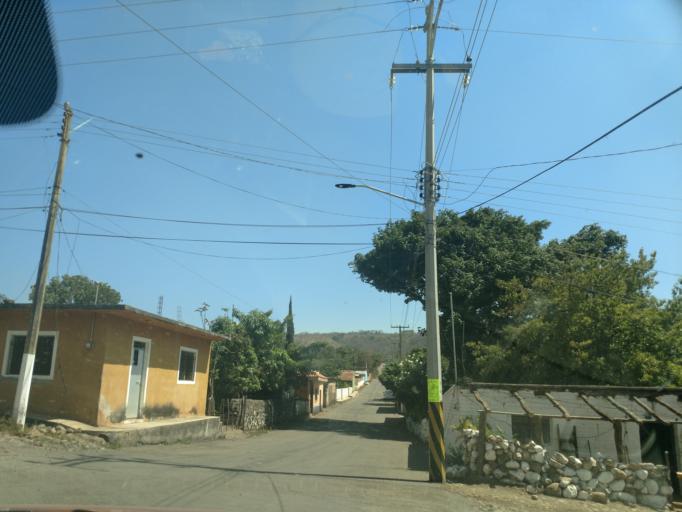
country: MX
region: Nayarit
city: Santa Maria del Oro
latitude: 21.4675
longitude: -104.6580
